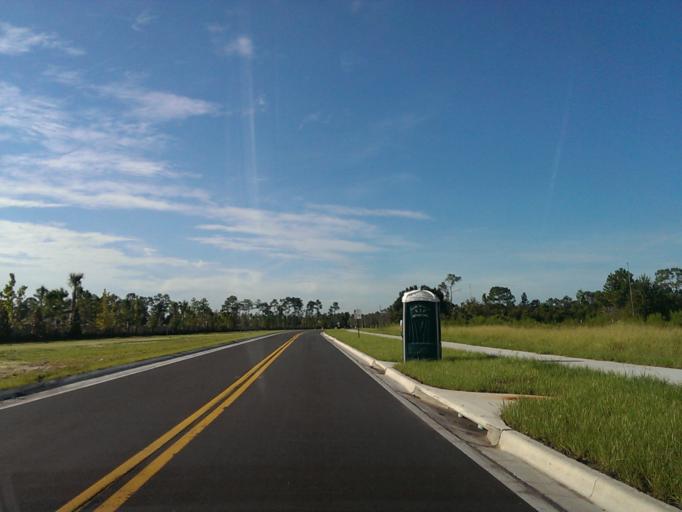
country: US
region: Florida
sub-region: Orange County
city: Lake Butler
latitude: 28.4447
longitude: -81.6011
